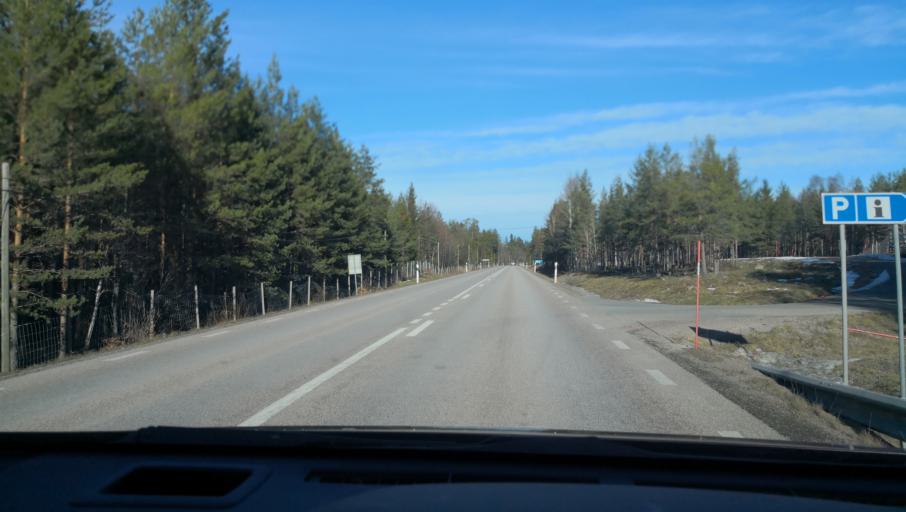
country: SE
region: Uppsala
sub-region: Uppsala Kommun
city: Vattholma
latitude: 60.1062
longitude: 17.7788
